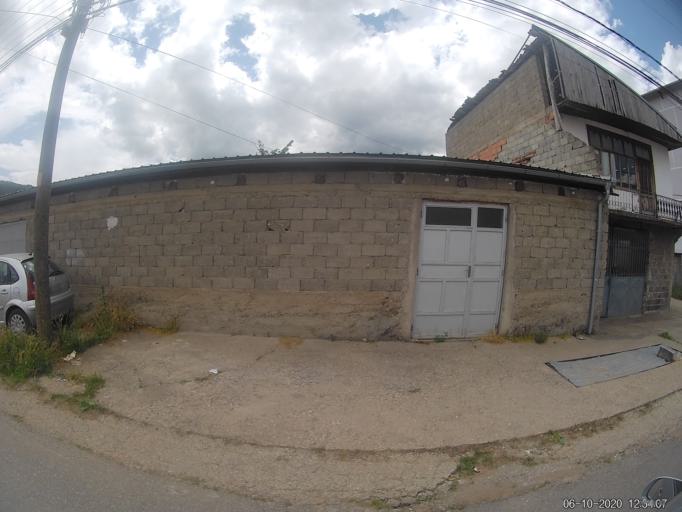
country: XK
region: Prizren
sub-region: Prizren
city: Prizren
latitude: 42.2383
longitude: 20.7680
